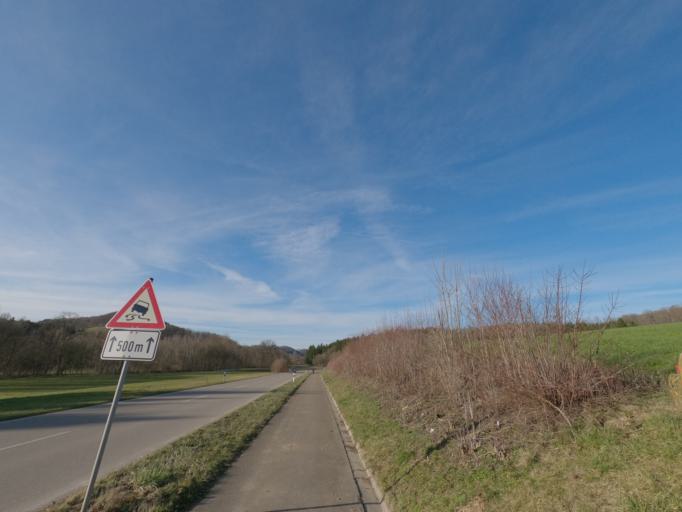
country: DE
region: Baden-Wuerttemberg
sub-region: Regierungsbezirk Stuttgart
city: Donzdorf
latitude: 48.6984
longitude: 9.8015
